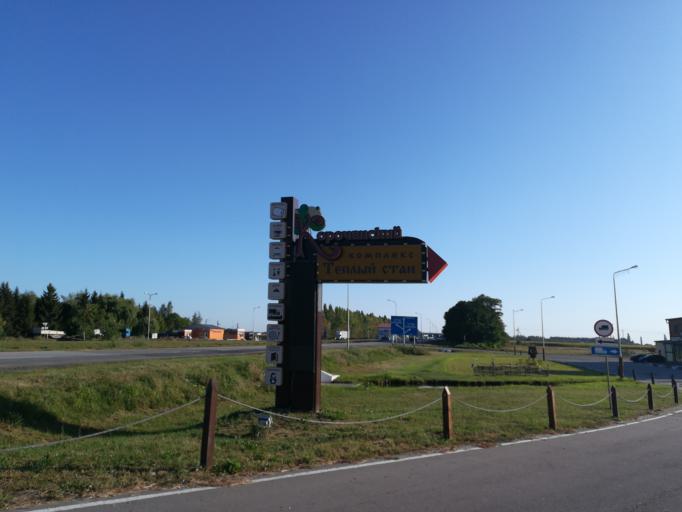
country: RU
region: Belgorod
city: Bekhteyevka
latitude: 50.7931
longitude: 37.1416
